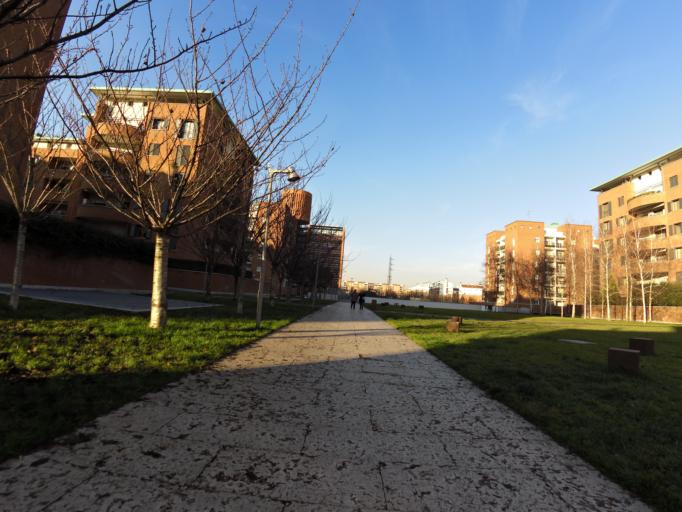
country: IT
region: Lombardy
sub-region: Citta metropolitana di Milano
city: Vimodrone
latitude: 45.5183
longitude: 9.2794
